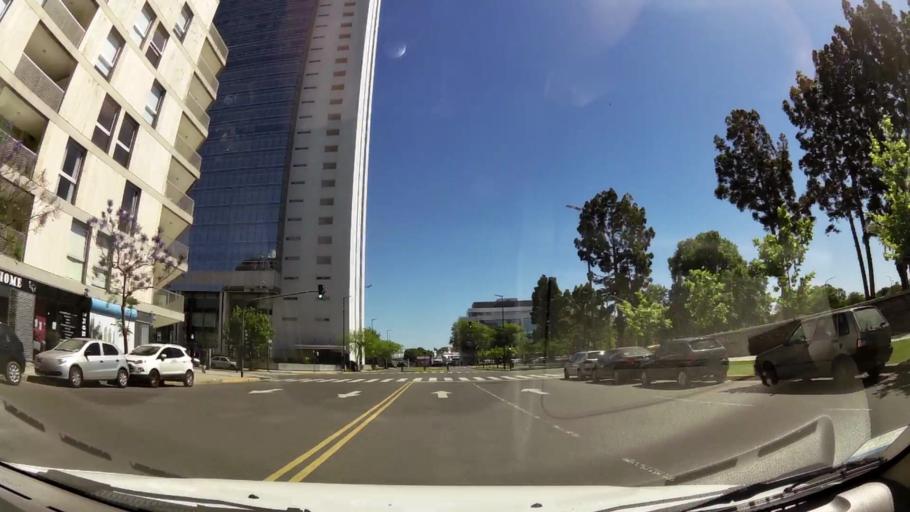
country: AR
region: Buenos Aires F.D.
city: Buenos Aires
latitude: -34.5992
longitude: -58.3638
